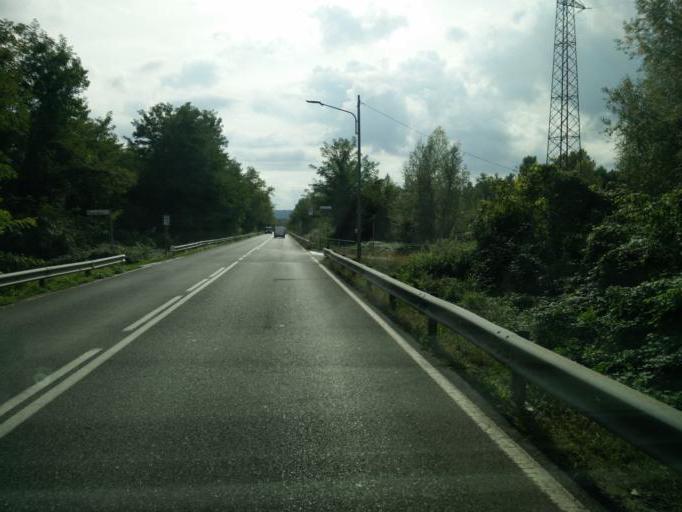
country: IT
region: Tuscany
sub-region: Provincia di Massa-Carrara
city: Filattiera
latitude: 44.3216
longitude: 9.9417
